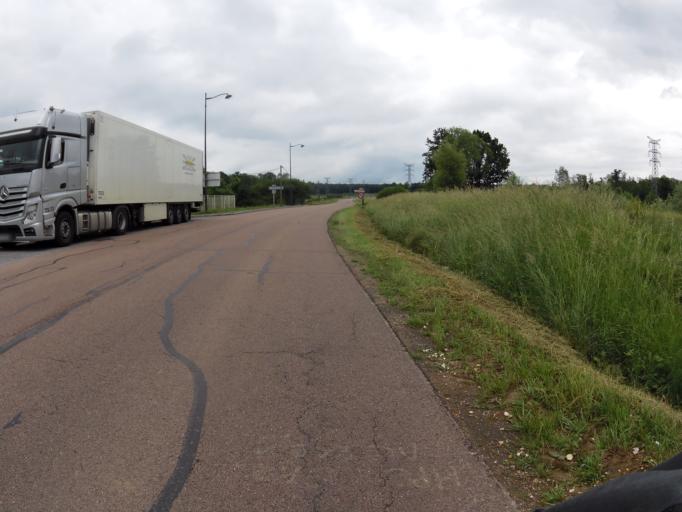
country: FR
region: Champagne-Ardenne
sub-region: Departement de la Haute-Marne
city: Saint-Dizier
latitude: 48.6529
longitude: 4.9353
